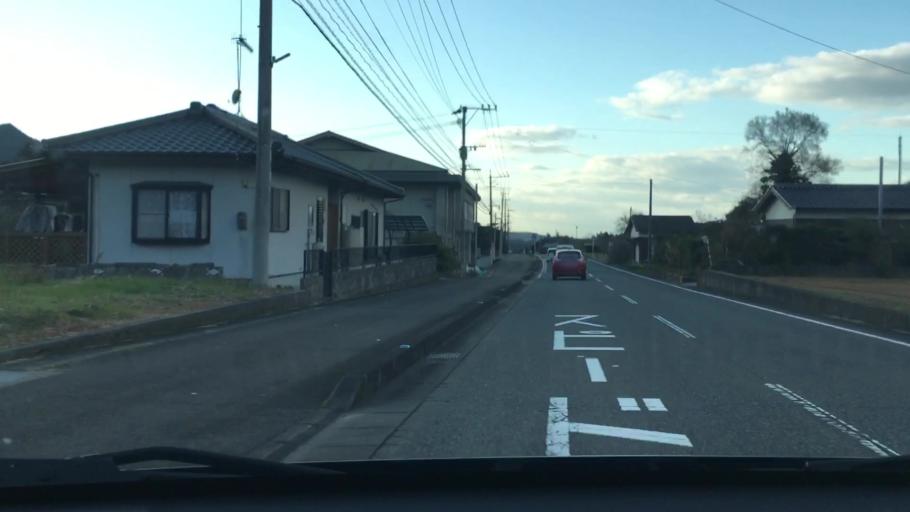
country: JP
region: Oita
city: Bungo-Takada-shi
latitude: 33.5019
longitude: 131.3722
